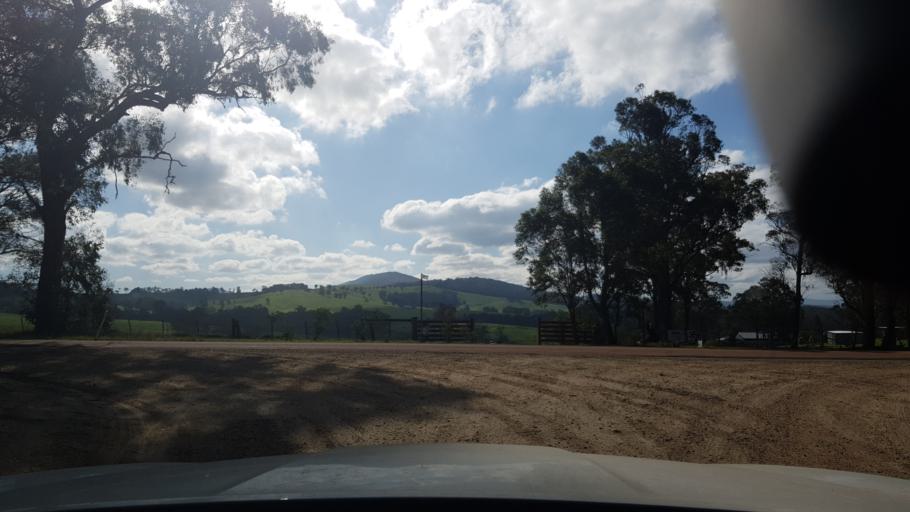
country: AU
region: Victoria
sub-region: East Gippsland
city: Bairnsdale
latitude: -37.7623
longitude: 147.5694
